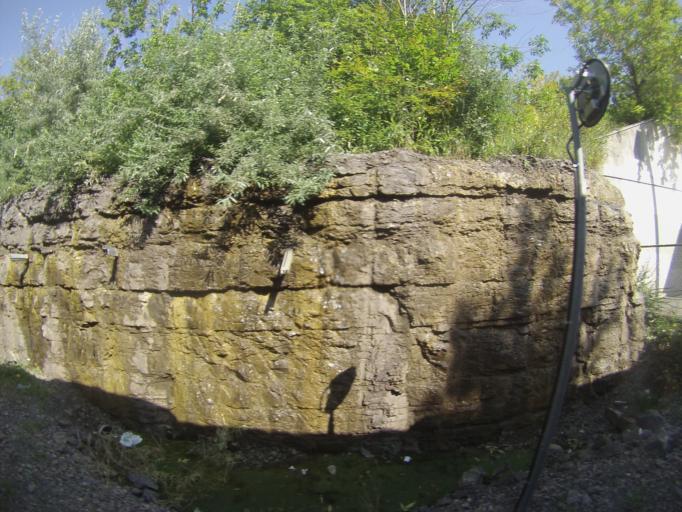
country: CA
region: Ontario
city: Ottawa
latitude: 45.3976
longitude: -75.7096
